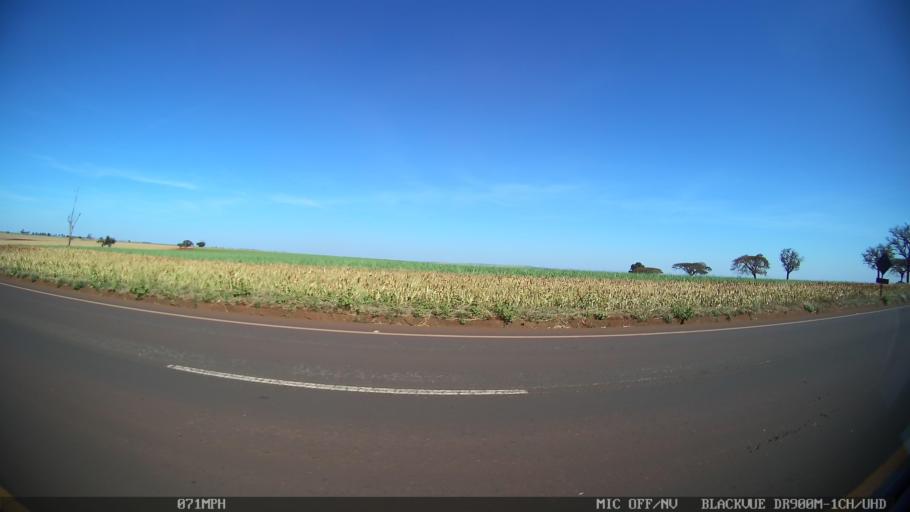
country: BR
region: Sao Paulo
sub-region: Ipua
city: Ipua
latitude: -20.4785
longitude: -48.0853
